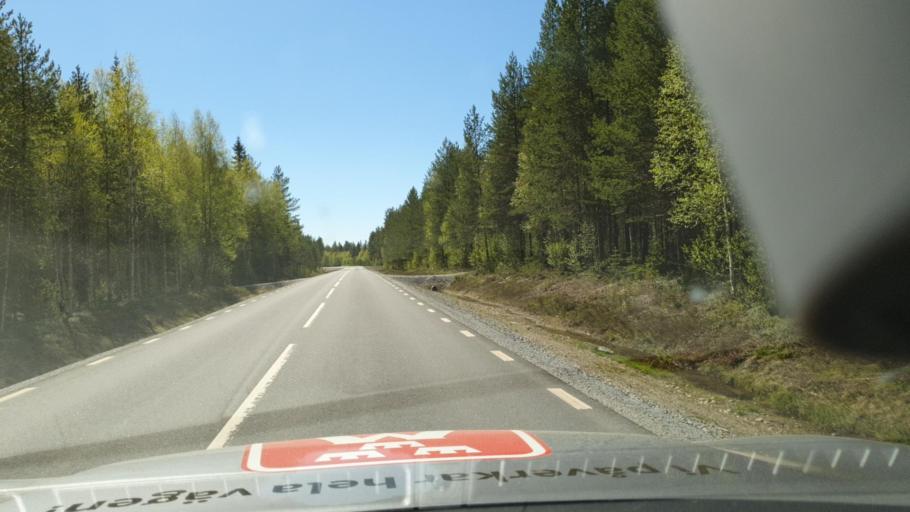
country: SE
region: Vaesternorrland
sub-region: OErnskoeldsviks Kommun
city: Bredbyn
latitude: 63.8750
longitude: 18.5002
